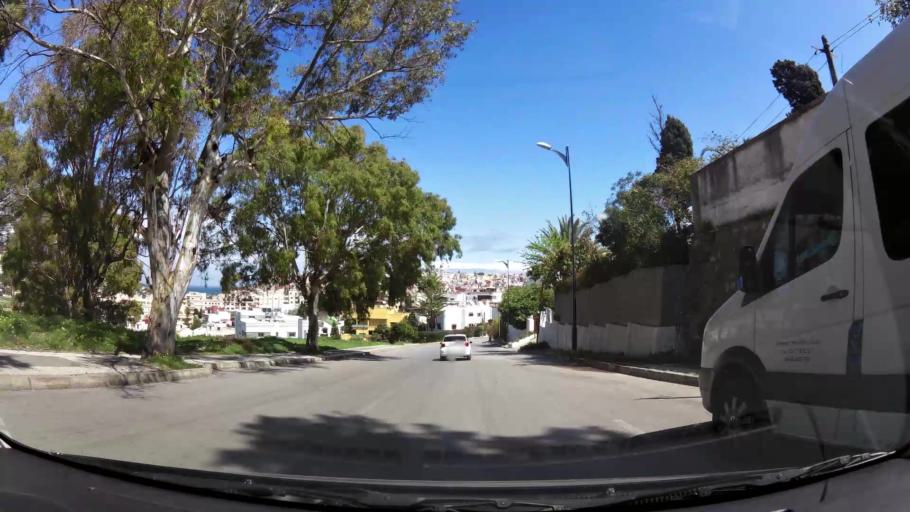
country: MA
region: Tanger-Tetouan
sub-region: Tanger-Assilah
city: Tangier
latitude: 35.7796
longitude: -5.8313
